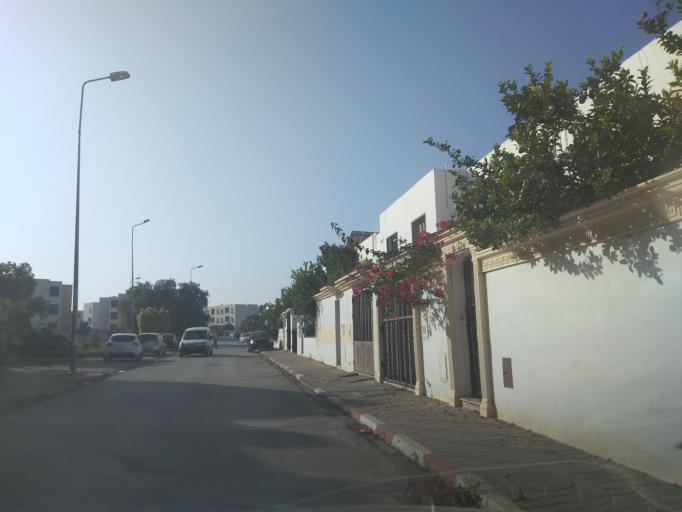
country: TN
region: Manouba
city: Manouba
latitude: 36.7910
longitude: 10.0856
